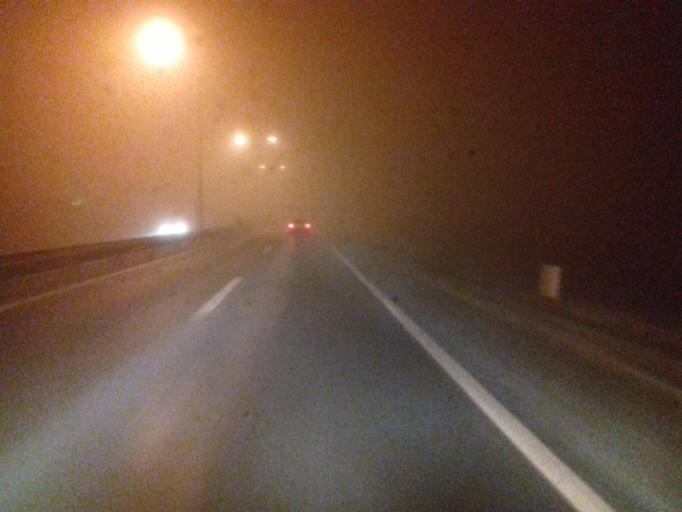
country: BA
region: Federation of Bosnia and Herzegovina
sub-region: Kanton Sarajevo
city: Sarajevo
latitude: 43.8357
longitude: 18.3065
